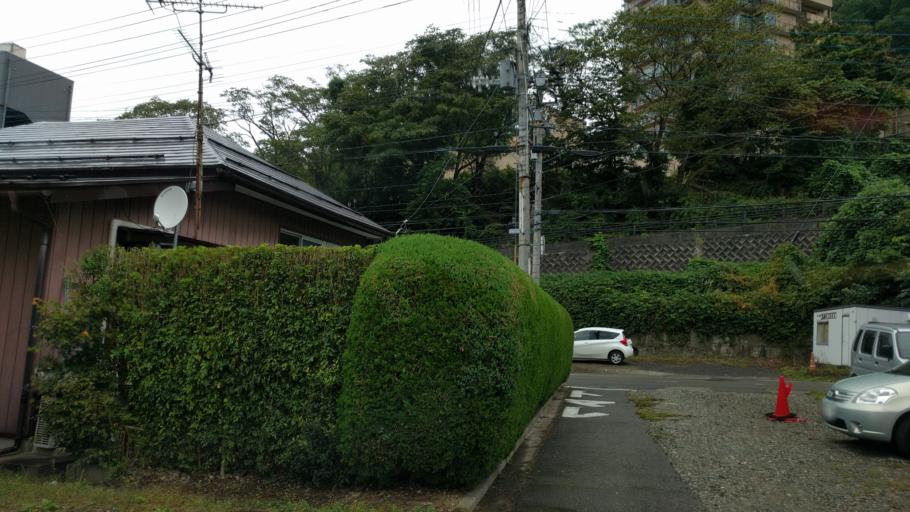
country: JP
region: Fukushima
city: Inawashiro
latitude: 37.4814
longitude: 139.9581
